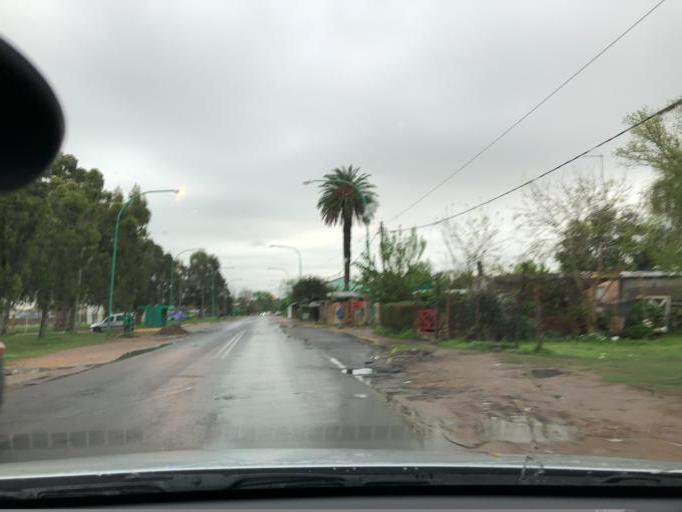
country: AR
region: Buenos Aires
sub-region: Partido de Ensenada
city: Ensenada
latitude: -34.8385
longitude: -57.9395
